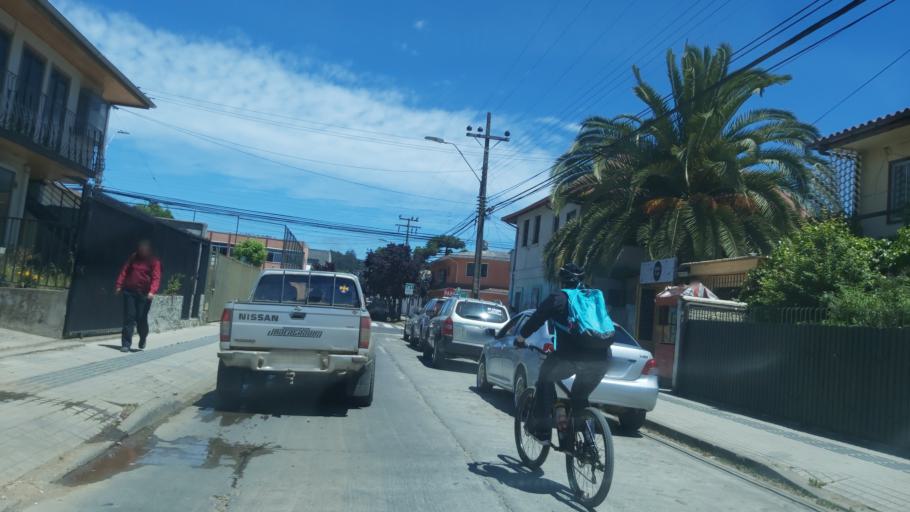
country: CL
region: Maule
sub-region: Provincia de Talca
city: Constitucion
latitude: -35.3288
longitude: -72.4093
